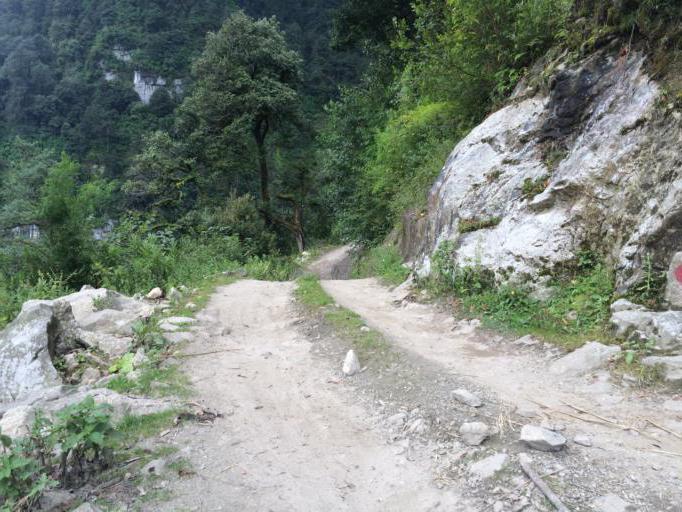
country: NP
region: Western Region
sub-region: Gandaki Zone
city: Chame
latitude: 28.5285
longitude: 84.3165
